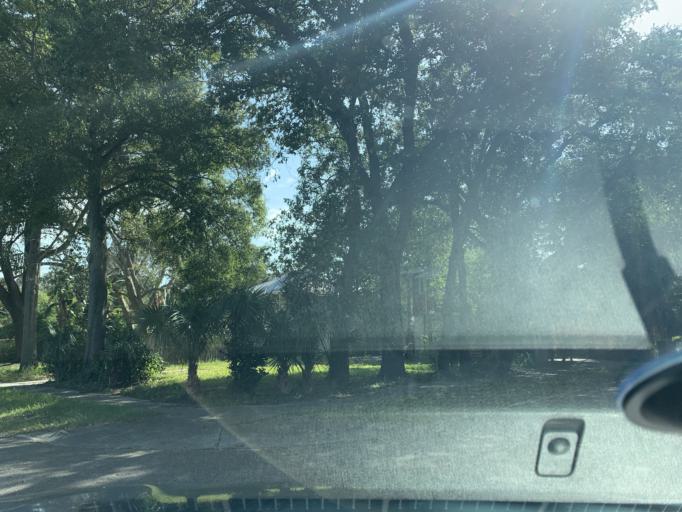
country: US
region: Florida
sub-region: Pinellas County
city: Saint Petersburg
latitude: 27.7570
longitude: -82.6424
